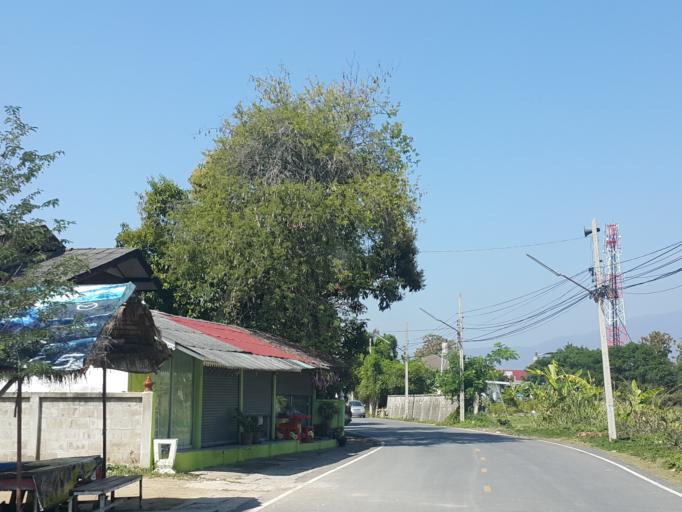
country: TH
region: Chiang Mai
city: Hang Dong
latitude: 18.7332
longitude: 98.9585
